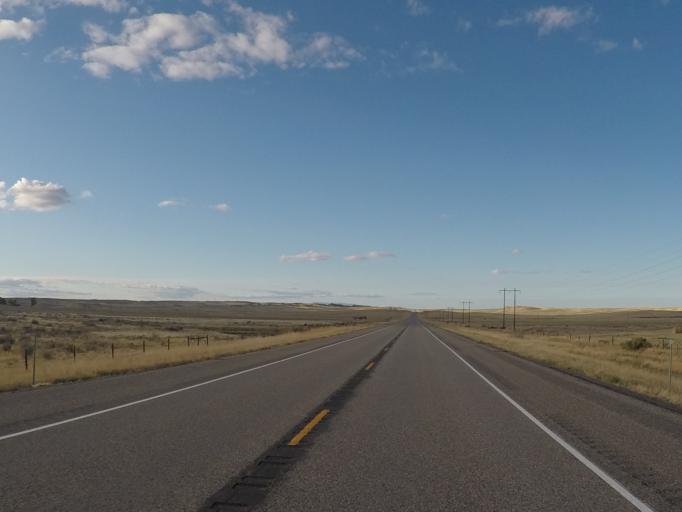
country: US
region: Montana
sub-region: Golden Valley County
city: Ryegate
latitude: 46.1991
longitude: -108.9182
